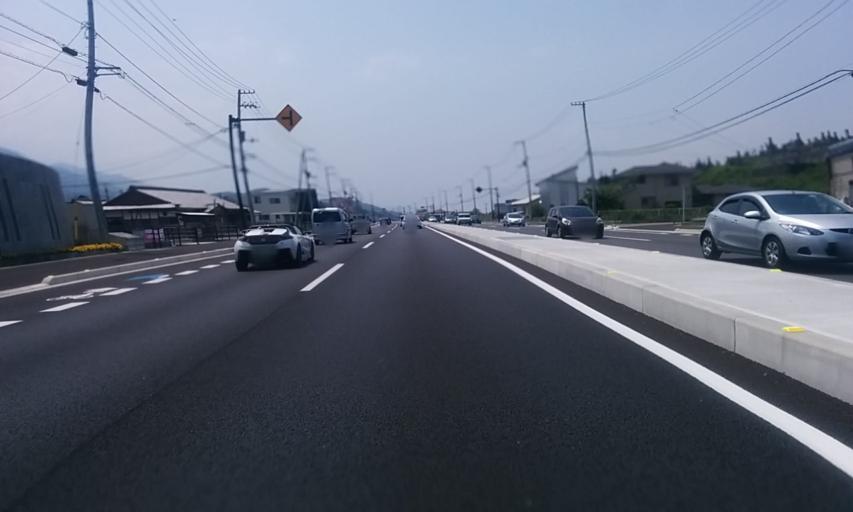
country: JP
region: Ehime
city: Niihama
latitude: 33.9254
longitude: 133.2590
